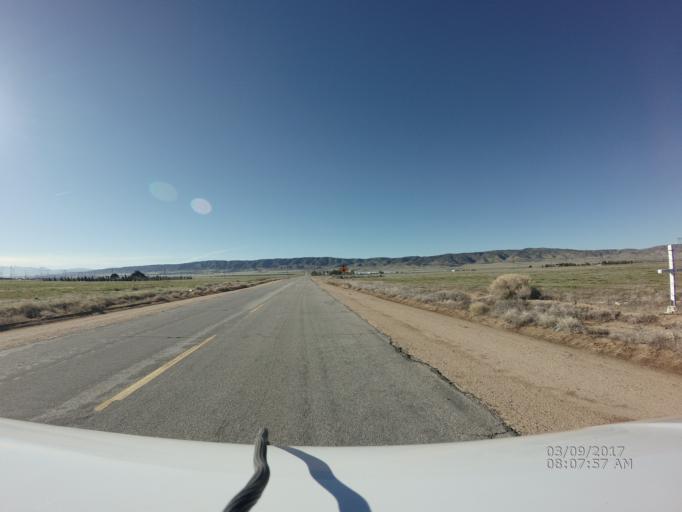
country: US
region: California
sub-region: Los Angeles County
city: Leona Valley
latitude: 34.7063
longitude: -118.3244
